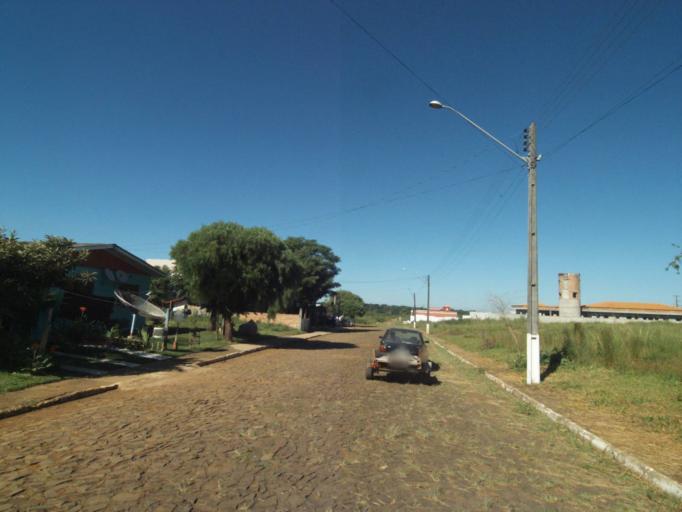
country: BR
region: Parana
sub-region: Pinhao
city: Pinhao
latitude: -25.8358
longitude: -52.0303
